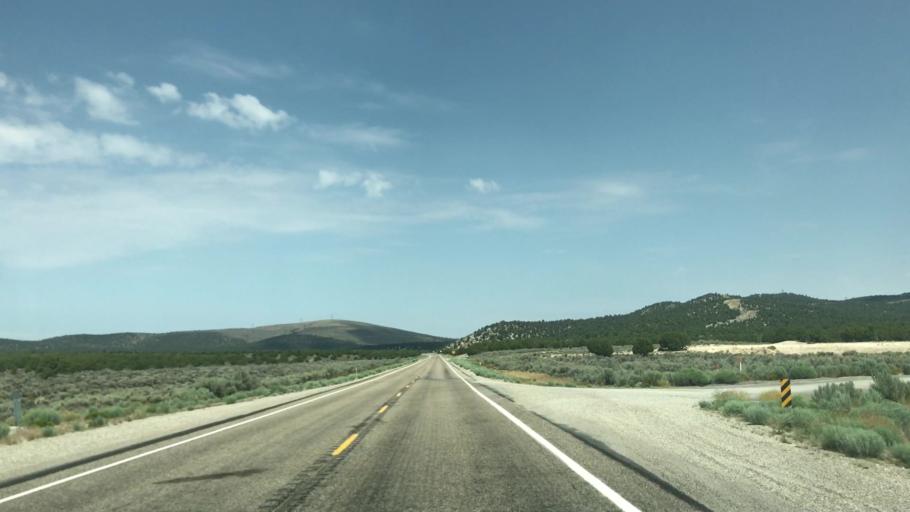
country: US
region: Nevada
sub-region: White Pine County
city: Ely
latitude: 39.3744
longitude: -115.0605
